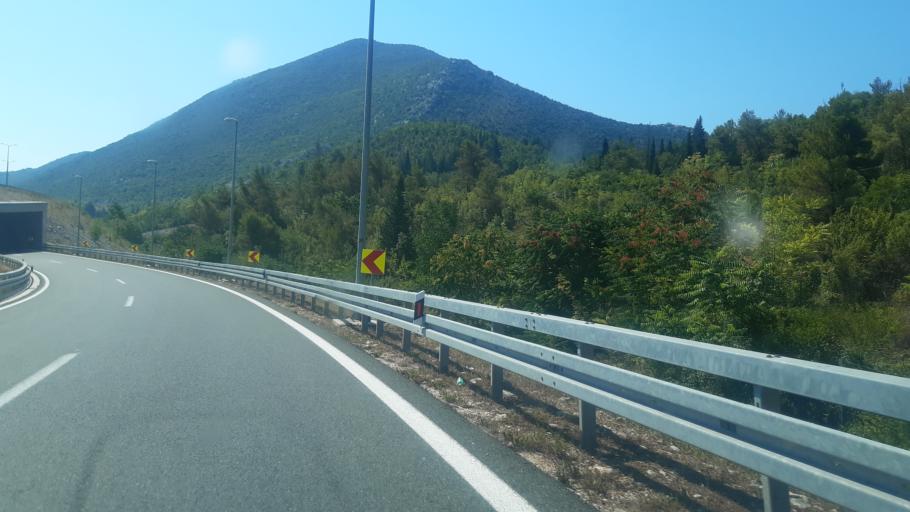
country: BA
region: Federation of Bosnia and Herzegovina
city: Ljubuski
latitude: 43.1487
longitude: 17.4837
